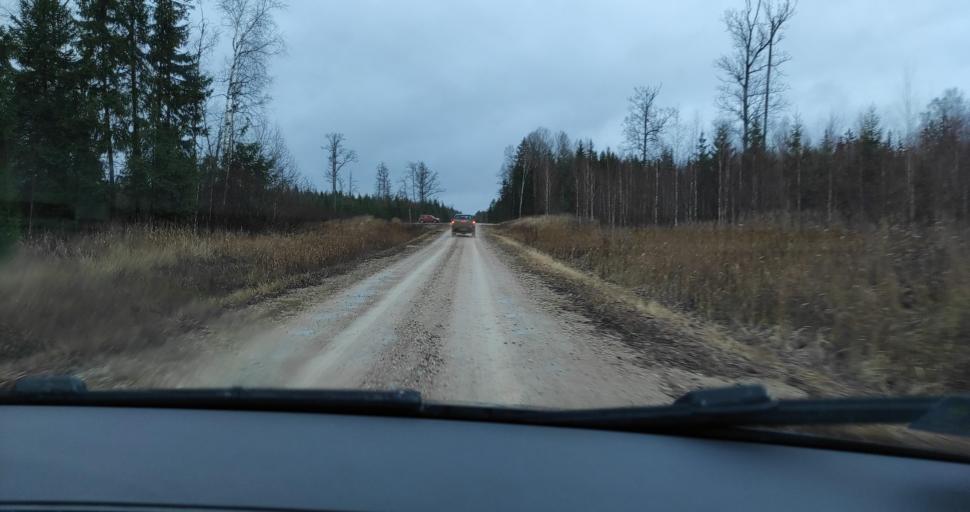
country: LV
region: Skrunda
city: Skrunda
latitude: 56.5631
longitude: 22.0789
